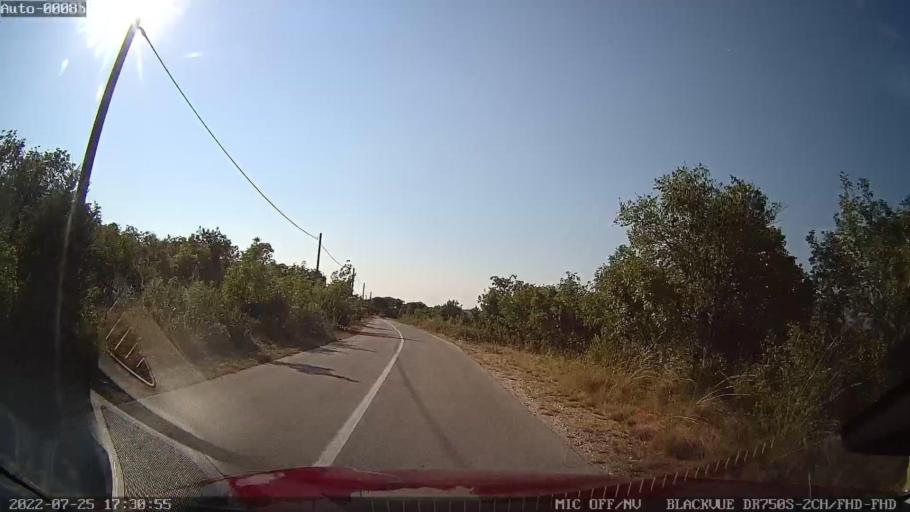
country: HR
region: Zadarska
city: Posedarje
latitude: 44.1673
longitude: 15.5041
